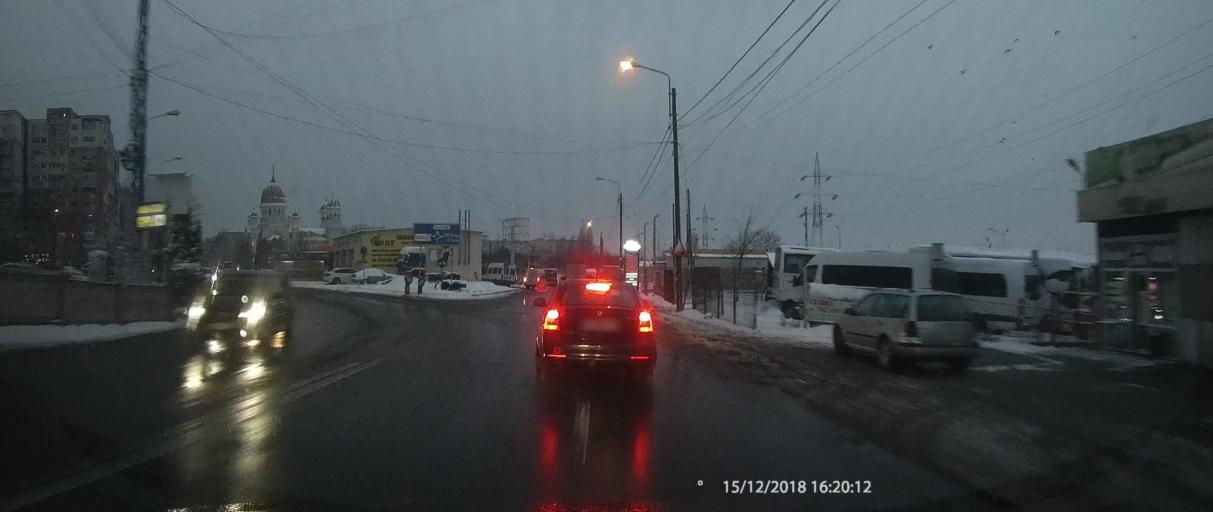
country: RO
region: Galati
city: Galati
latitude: 45.4144
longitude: 28.0050
